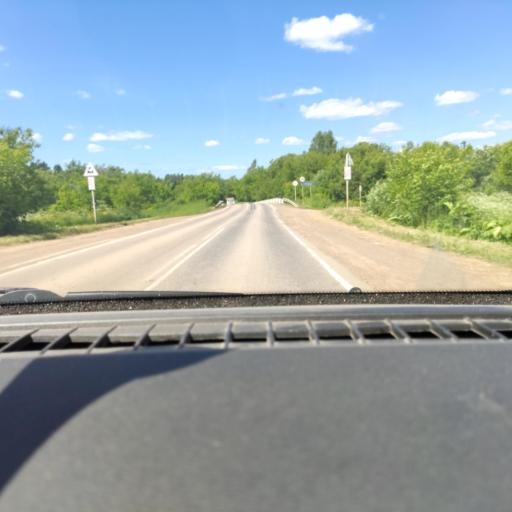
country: RU
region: Perm
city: Chaykovskaya
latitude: 58.1101
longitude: 55.5856
